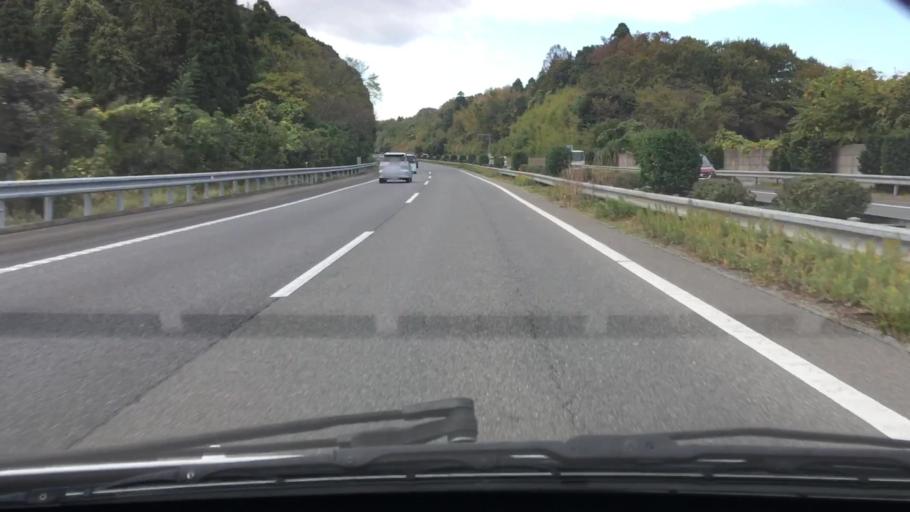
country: JP
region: Chiba
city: Ichihara
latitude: 35.4385
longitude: 140.0558
